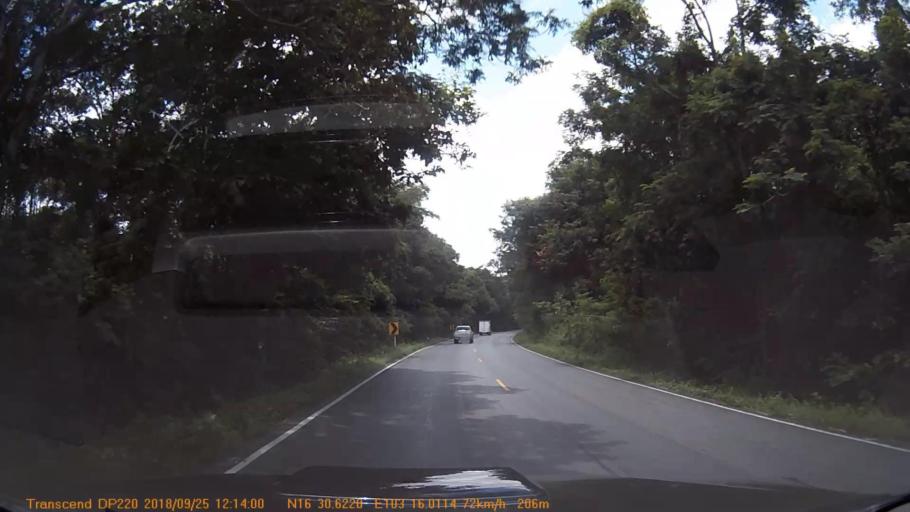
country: TH
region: Kalasin
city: Huai Mek
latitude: 16.5105
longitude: 103.2668
